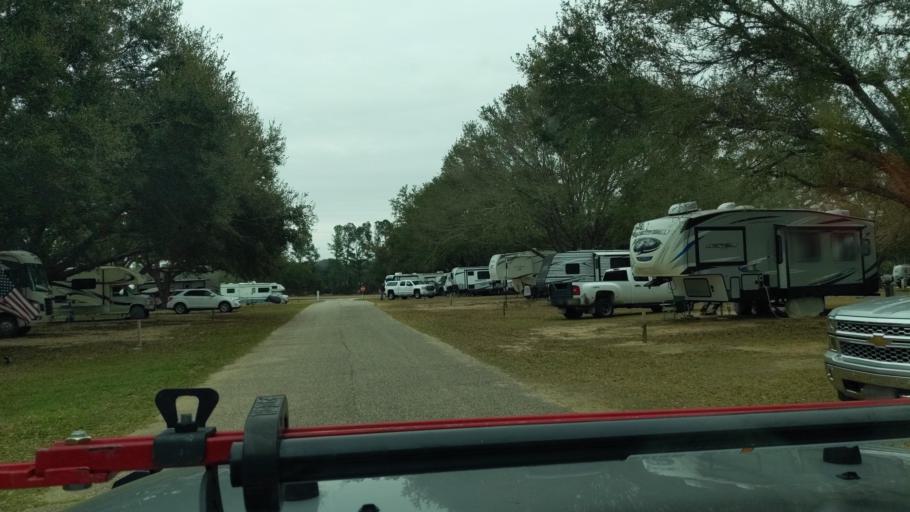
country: US
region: Alabama
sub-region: Baldwin County
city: Foley
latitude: 30.4590
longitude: -87.7807
